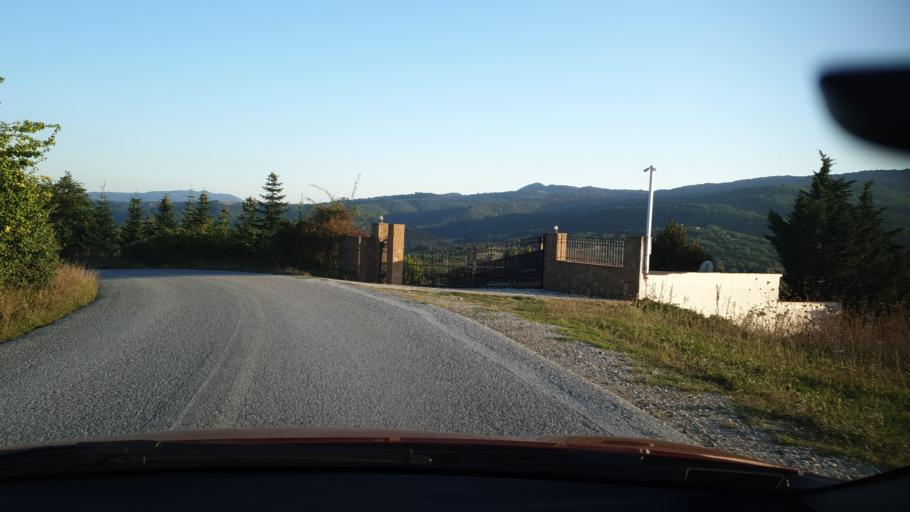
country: GR
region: Central Macedonia
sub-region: Nomos Chalkidikis
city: Galatista
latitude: 40.5299
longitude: 23.2762
